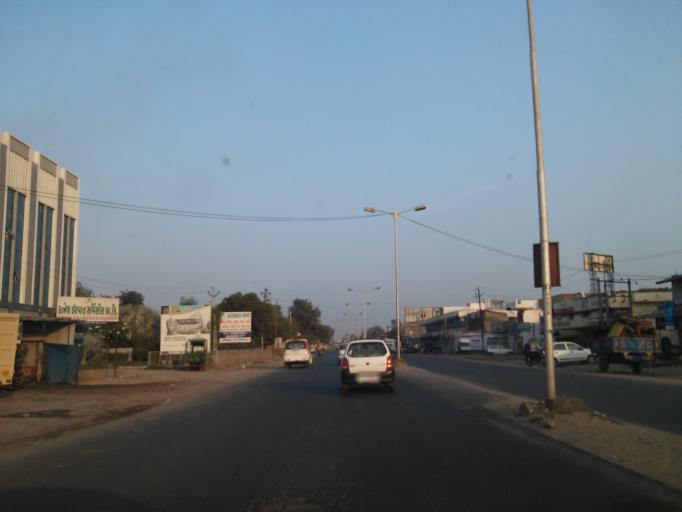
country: IN
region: Gujarat
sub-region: Ahmadabad
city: Sarkhej
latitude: 22.9873
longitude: 72.4922
